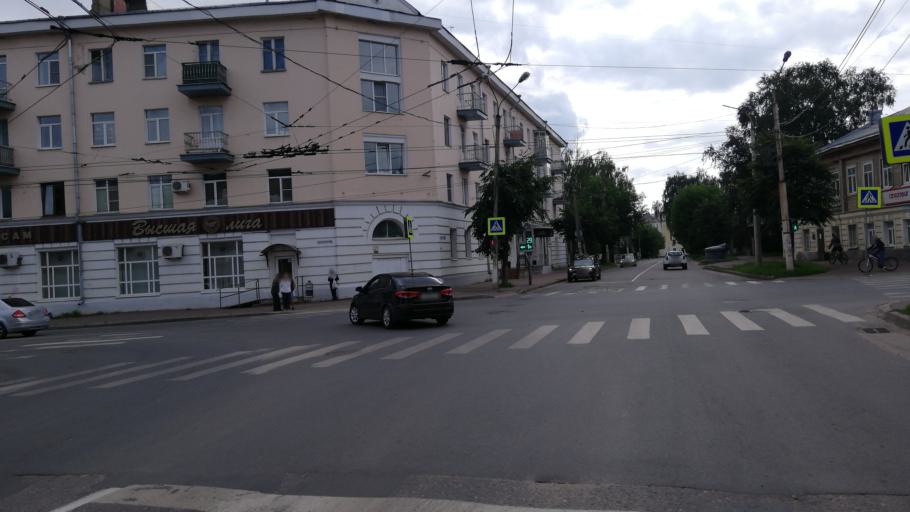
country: RU
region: Kostroma
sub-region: Kostromskoy Rayon
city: Kostroma
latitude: 57.7709
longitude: 40.9221
